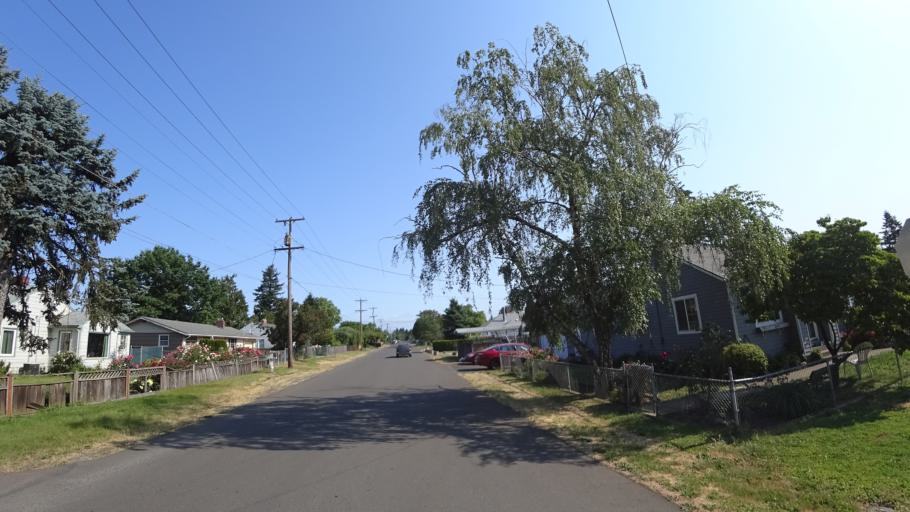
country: US
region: Oregon
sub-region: Multnomah County
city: Lents
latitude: 45.4600
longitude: -122.5946
